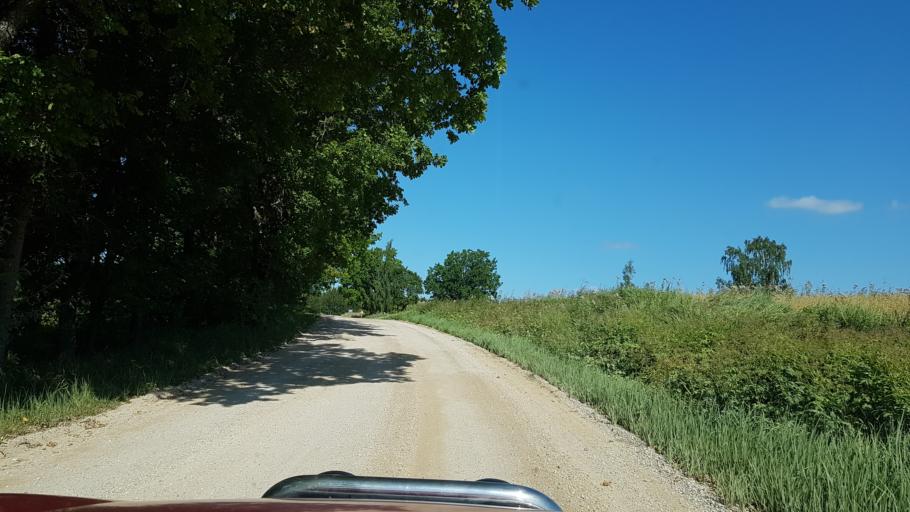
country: RU
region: Pskov
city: Pechory
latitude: 57.7669
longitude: 27.3218
